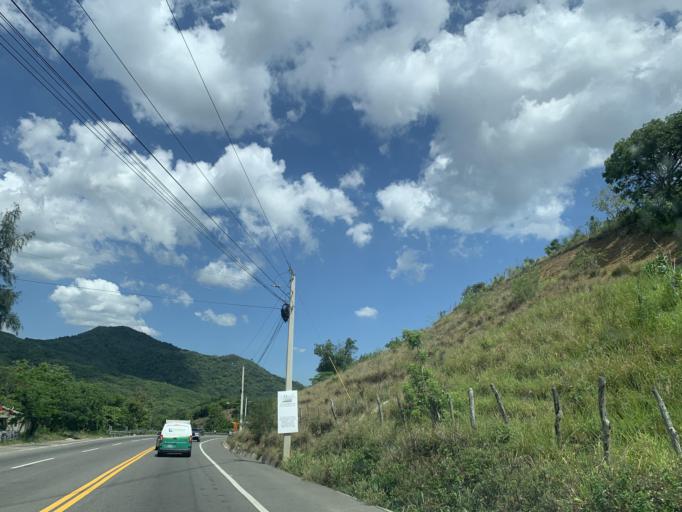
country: DO
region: Puerto Plata
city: Altamira
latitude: 19.6188
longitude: -70.8438
